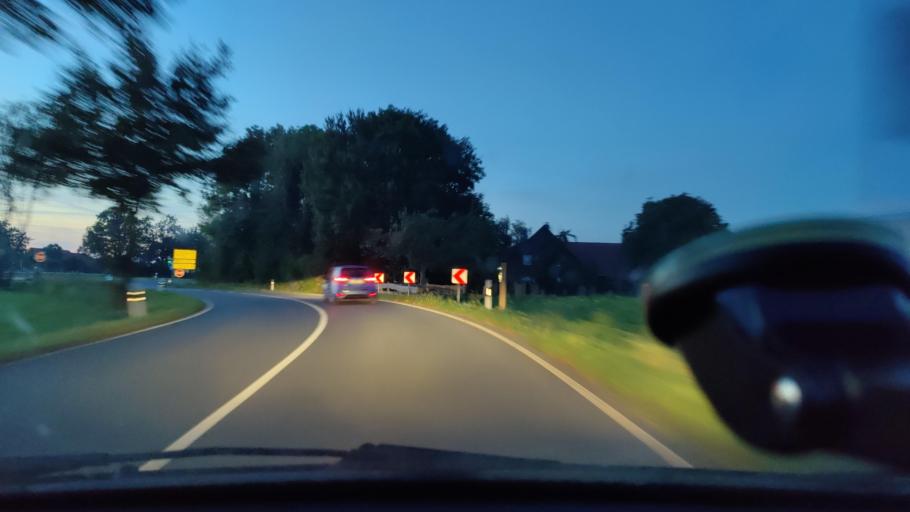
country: DE
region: North Rhine-Westphalia
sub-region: Regierungsbezirk Munster
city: Sudlohn
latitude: 51.9202
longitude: 6.8488
